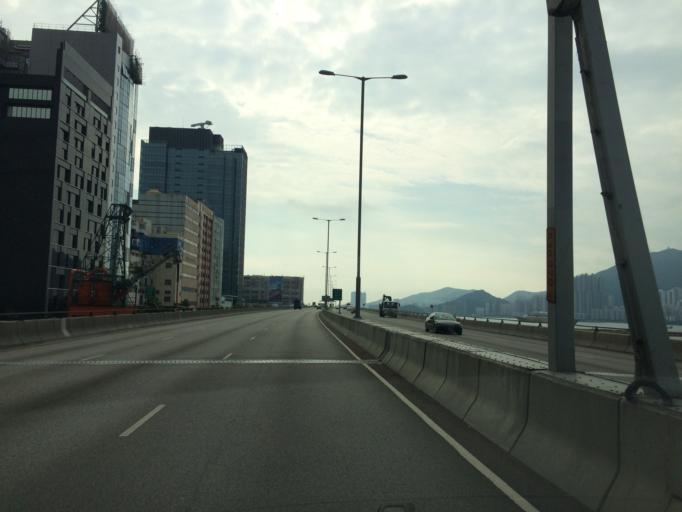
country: HK
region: Kowloon City
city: Kowloon
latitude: 22.3115
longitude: 114.2181
